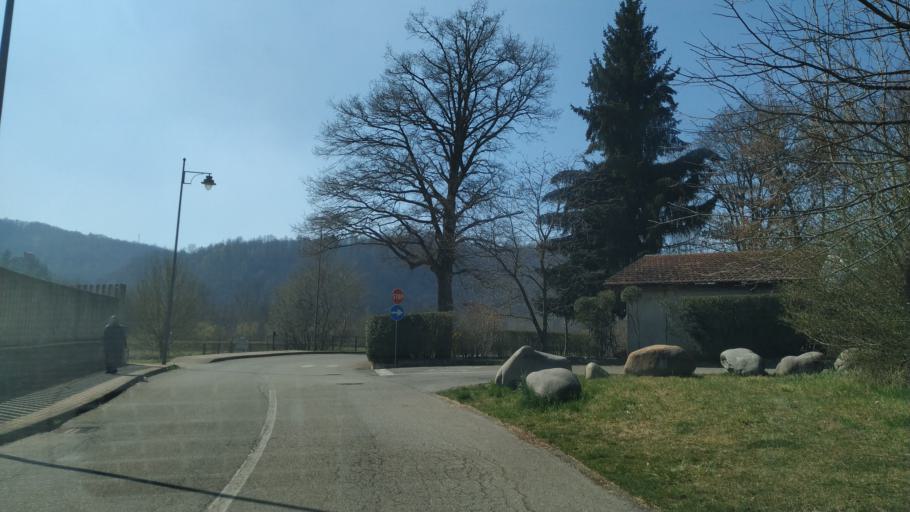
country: IT
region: Piedmont
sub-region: Provincia di Biella
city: Pray
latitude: 45.6749
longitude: 8.2149
